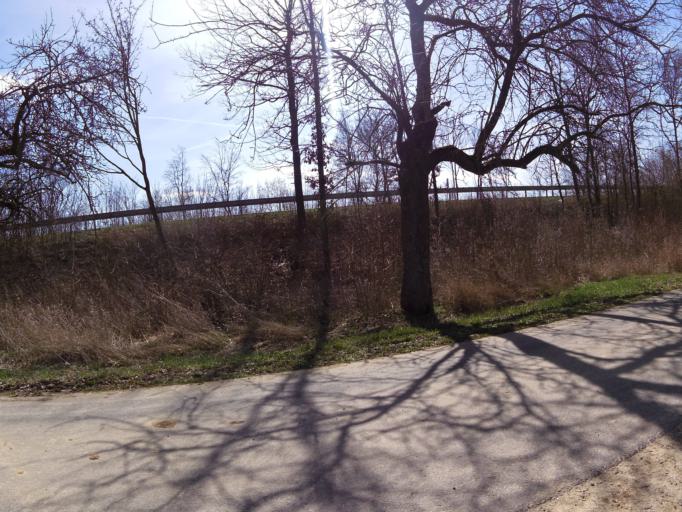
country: DE
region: Bavaria
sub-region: Regierungsbezirk Unterfranken
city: Biebelried
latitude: 49.7884
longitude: 10.0990
